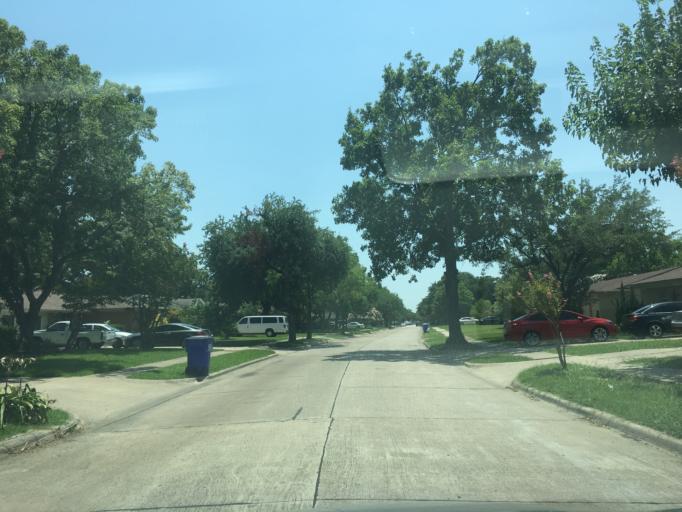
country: US
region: Texas
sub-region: Dallas County
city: Farmers Branch
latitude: 32.9346
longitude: -96.8807
